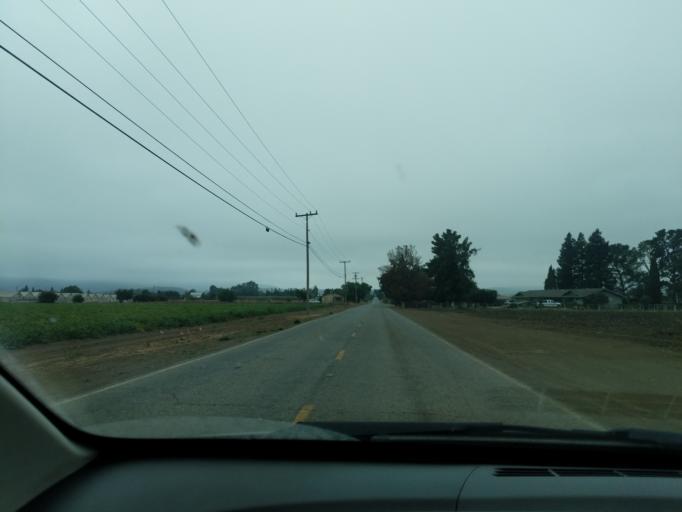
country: US
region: California
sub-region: Santa Clara County
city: Gilroy
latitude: 37.0473
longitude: -121.5646
